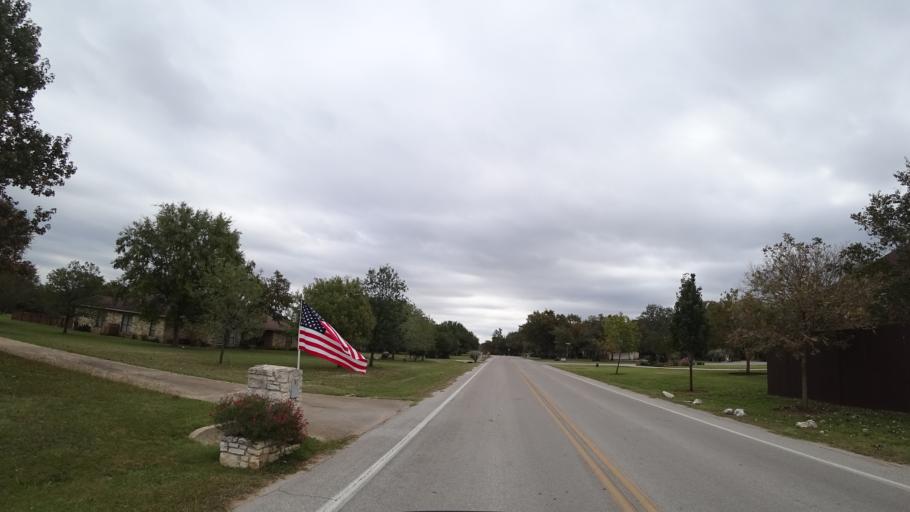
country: US
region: Texas
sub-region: Travis County
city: Shady Hollow
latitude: 30.1569
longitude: -97.8717
